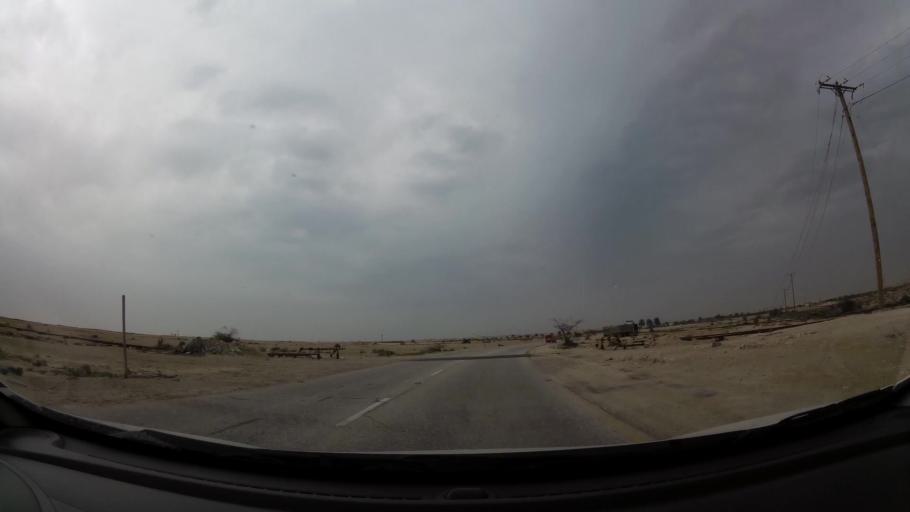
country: BH
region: Central Governorate
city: Dar Kulayb
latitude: 26.0779
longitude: 50.5452
